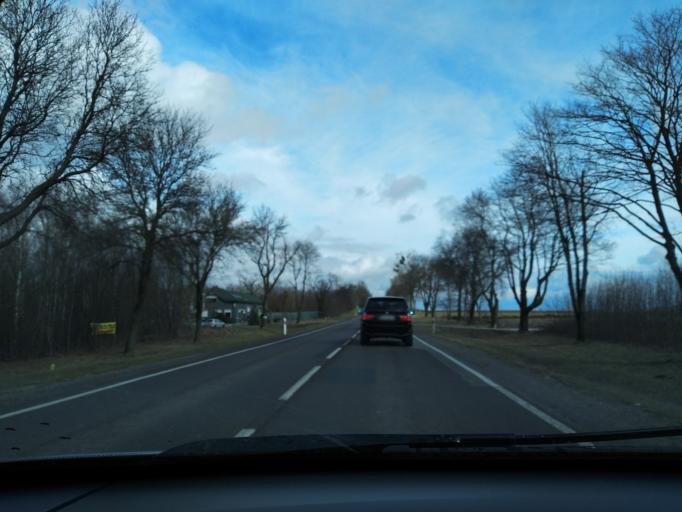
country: PL
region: Lodz Voivodeship
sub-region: Powiat zgierski
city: Strykow
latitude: 51.8667
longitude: 19.5148
